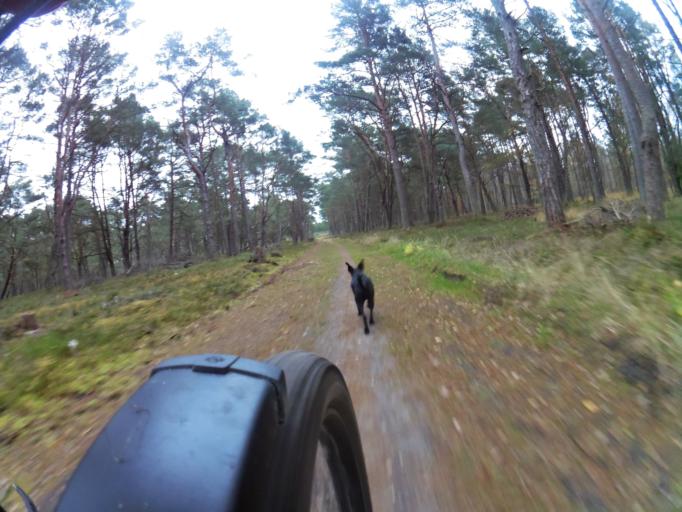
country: PL
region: Pomeranian Voivodeship
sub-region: Powiat leborski
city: Leba
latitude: 54.7782
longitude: 17.7135
